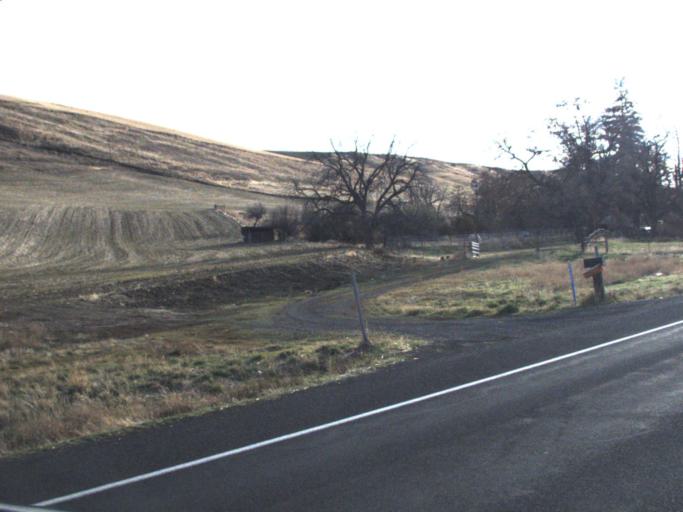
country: US
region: Washington
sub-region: Columbia County
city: Dayton
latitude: 46.3096
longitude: -117.9964
